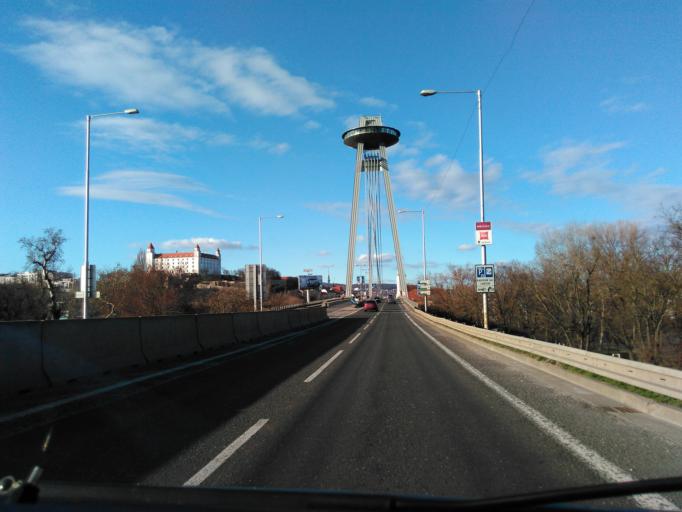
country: SK
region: Bratislavsky
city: Bratislava
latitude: 48.1345
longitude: 17.1048
